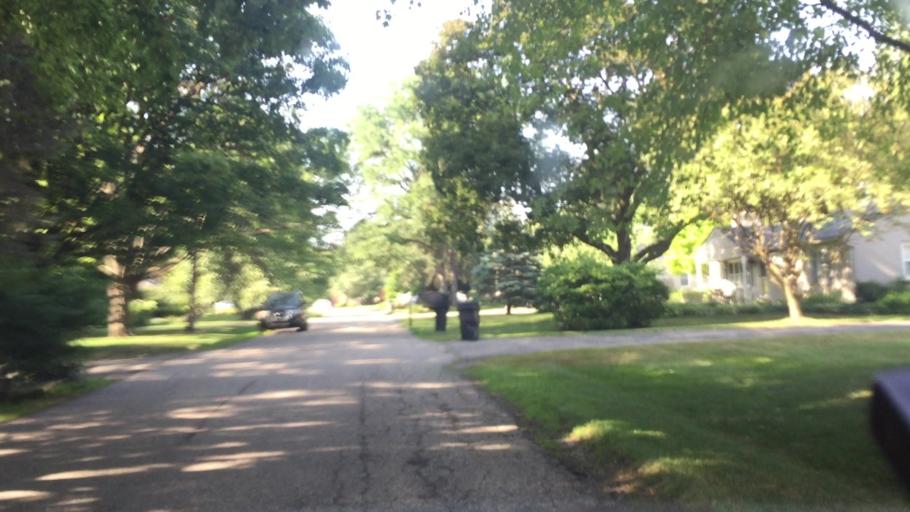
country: US
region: Michigan
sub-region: Oakland County
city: Franklin
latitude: 42.5452
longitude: -83.2929
